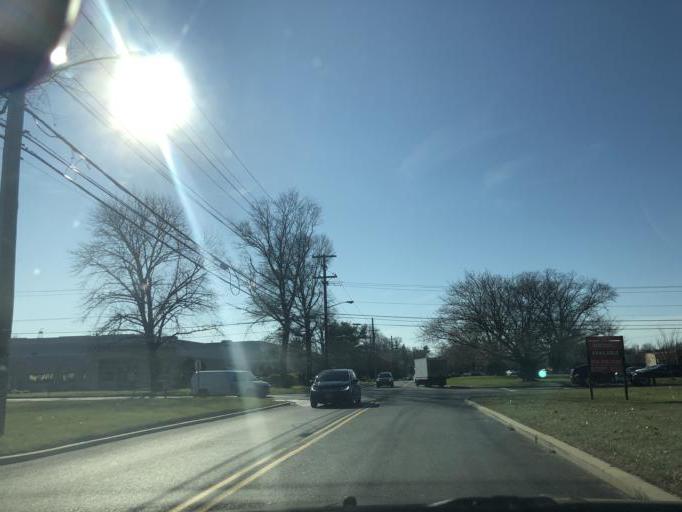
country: US
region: New Jersey
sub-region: Burlington County
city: Moorestown-Lenola
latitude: 39.9674
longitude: -74.9713
